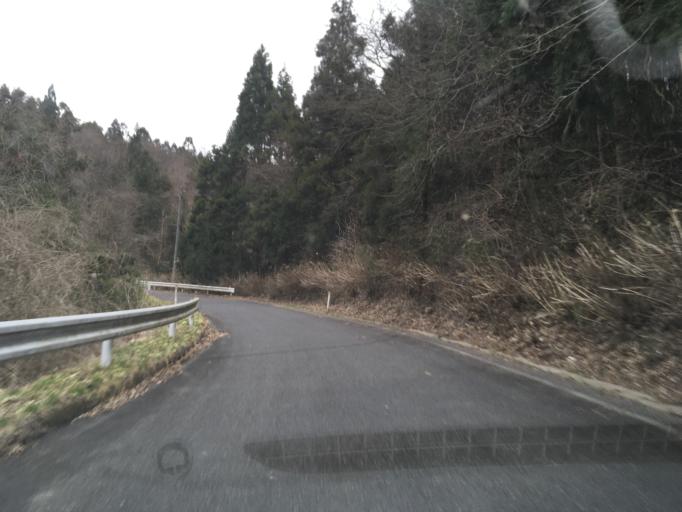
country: JP
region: Iwate
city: Ichinoseki
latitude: 38.7599
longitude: 141.2240
